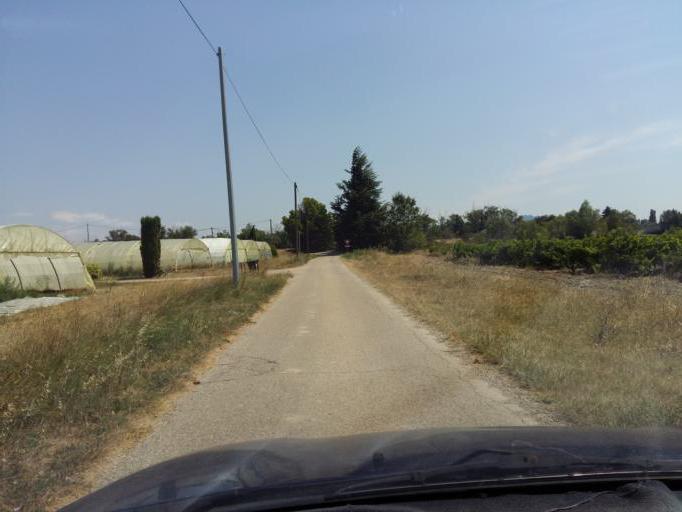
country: FR
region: Provence-Alpes-Cote d'Azur
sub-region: Departement du Vaucluse
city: Camaret-sur-Aigues
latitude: 44.1902
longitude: 4.8878
